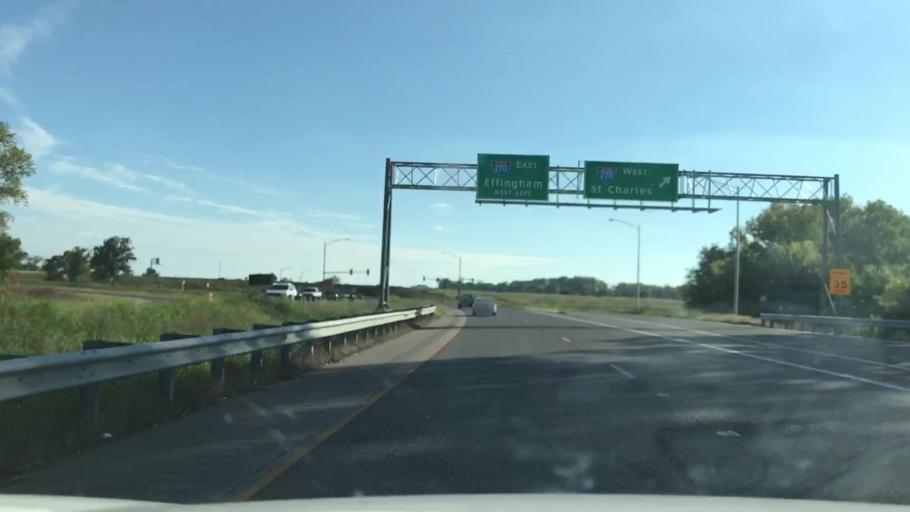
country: US
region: Illinois
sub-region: Madison County
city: Mitchell
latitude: 38.7698
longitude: -90.1224
